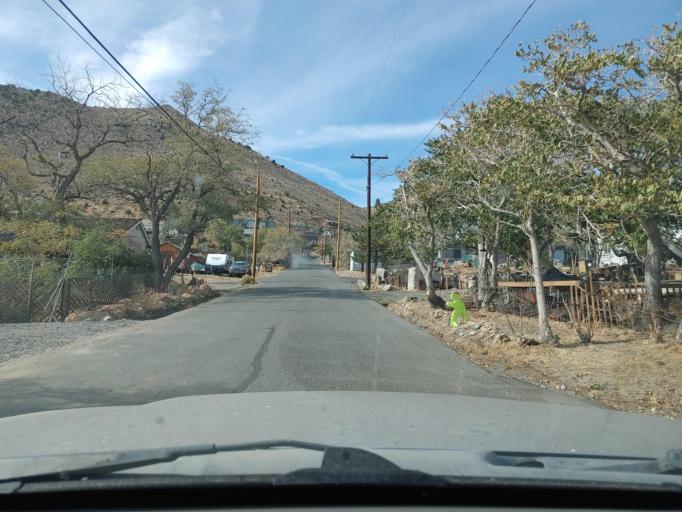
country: US
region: Nevada
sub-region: Storey County
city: Virginia City
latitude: 39.3081
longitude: -119.6466
